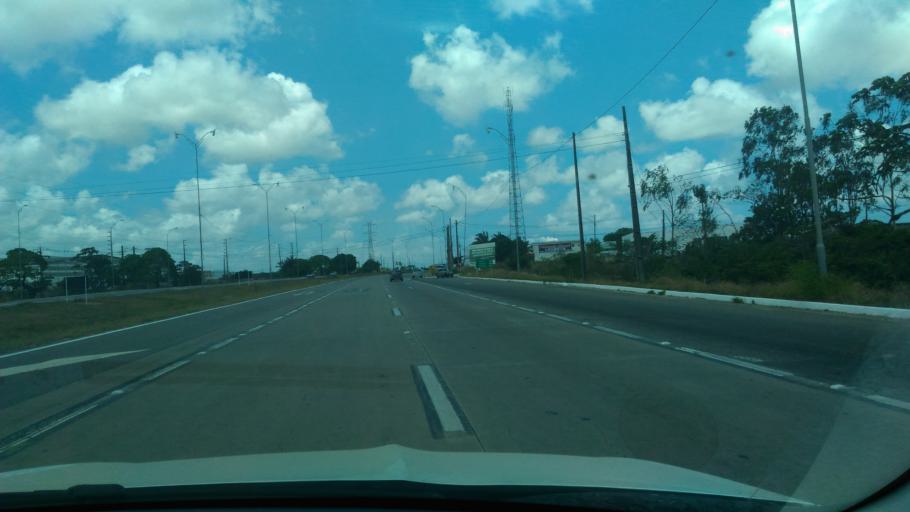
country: BR
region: Paraiba
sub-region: Conde
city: Conde
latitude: -7.2607
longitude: -34.9358
